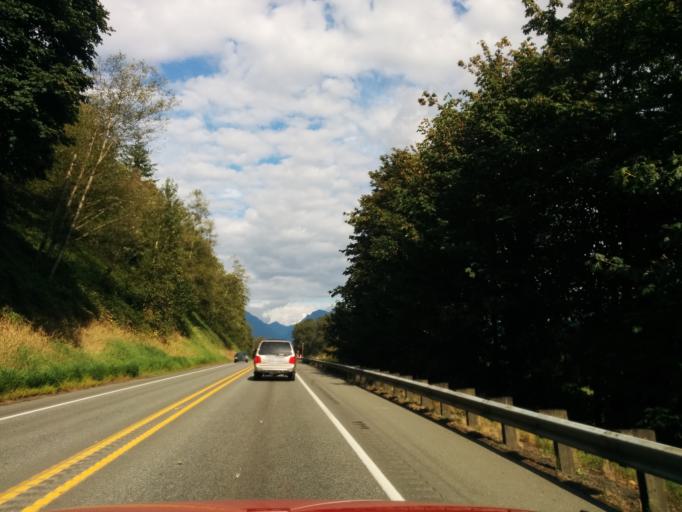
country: US
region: Washington
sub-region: Snohomish County
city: Sultan
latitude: 47.8516
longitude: -121.8566
